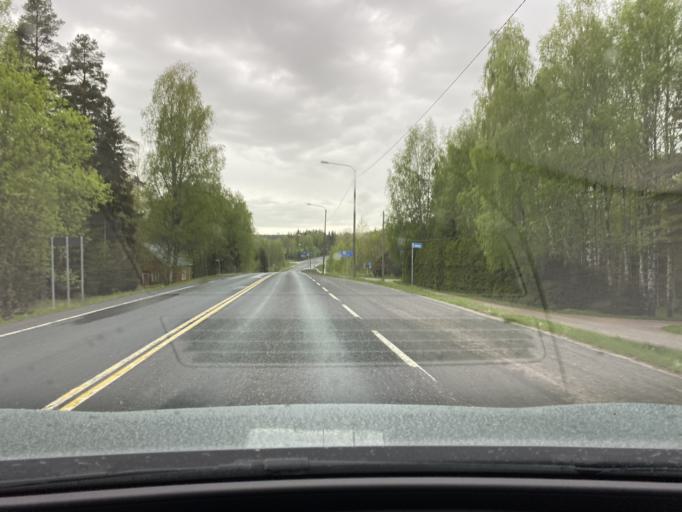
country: FI
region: Varsinais-Suomi
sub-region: Salo
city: Suomusjaervi
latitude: 60.3703
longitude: 23.6925
